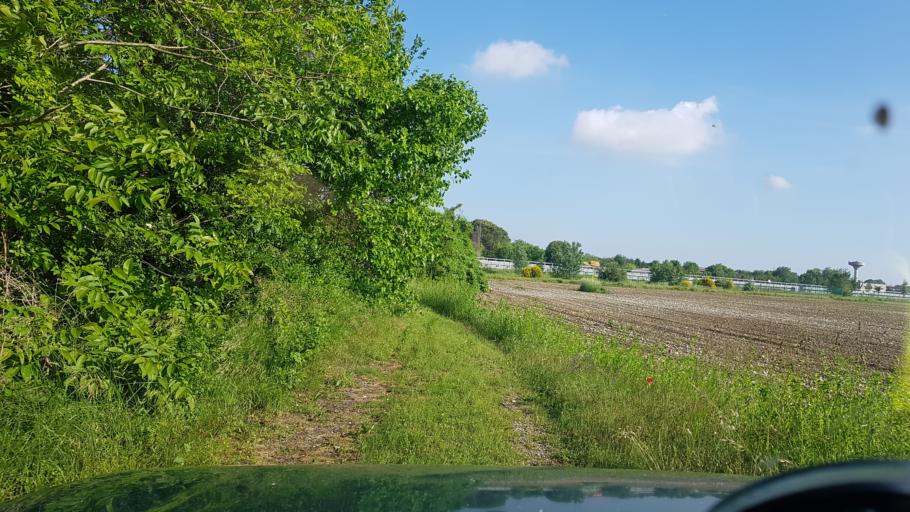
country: IT
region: Friuli Venezia Giulia
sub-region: Provincia di Gorizia
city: Romans d'Isonzo
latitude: 45.8801
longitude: 13.4591
